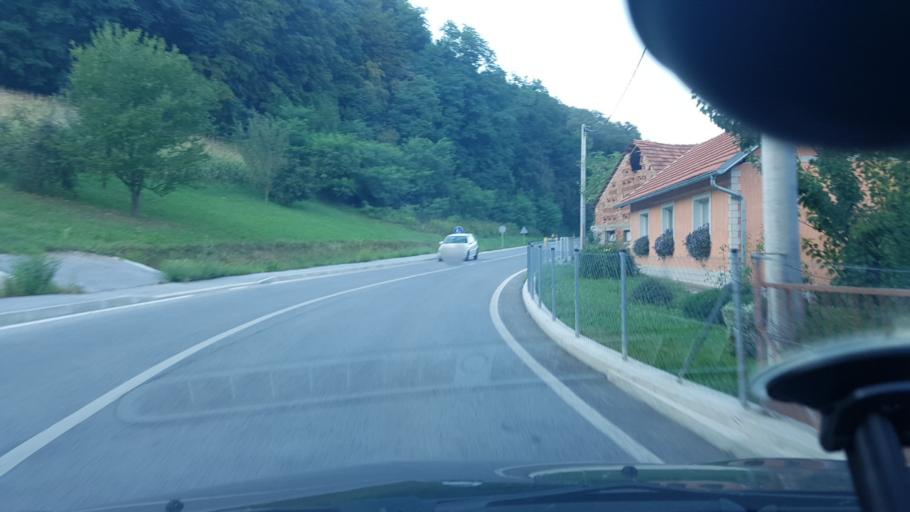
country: HR
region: Krapinsko-Zagorska
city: Pregrada
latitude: 46.1522
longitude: 15.7914
